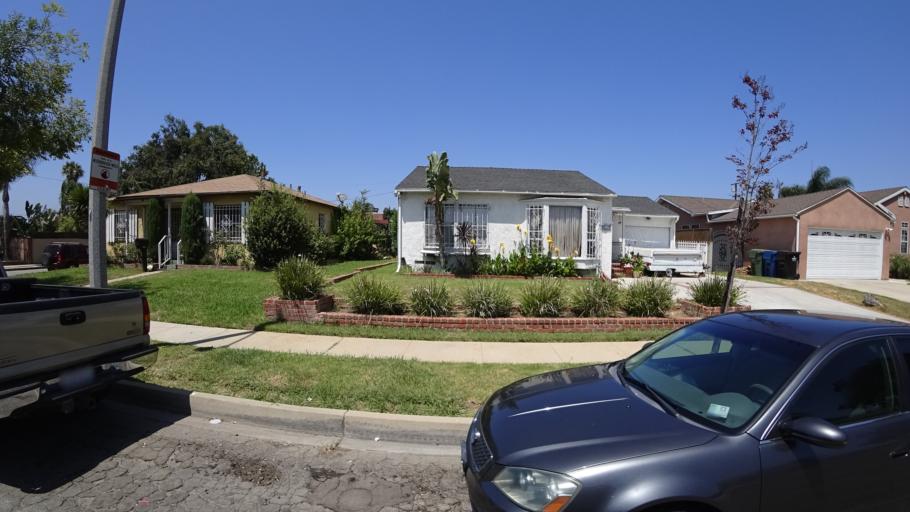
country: US
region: California
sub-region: Los Angeles County
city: Lennox
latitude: 33.9280
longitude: -118.3370
